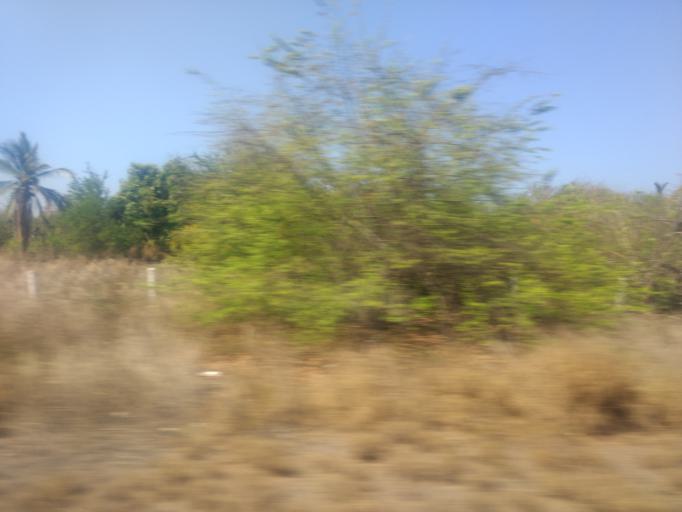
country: MX
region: Colima
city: El Colomo
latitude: 18.9605
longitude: -104.1482
